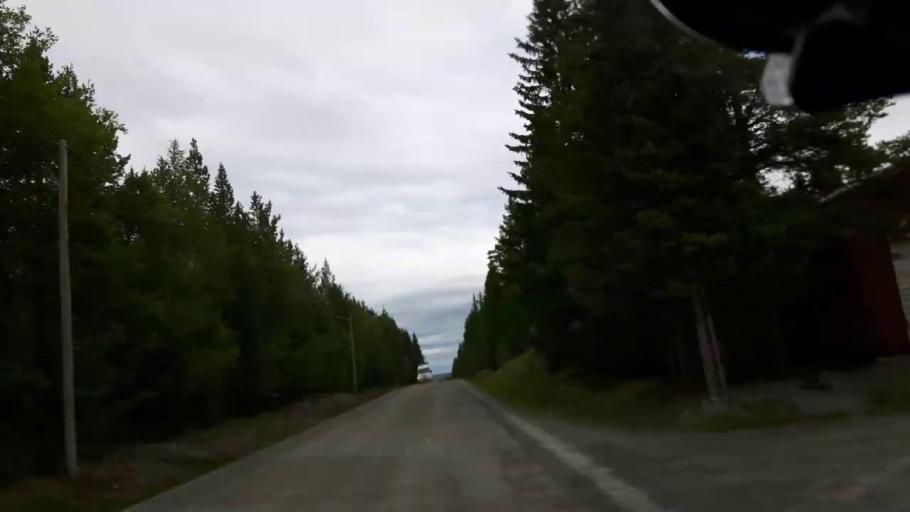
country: SE
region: Jaemtland
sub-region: OEstersunds Kommun
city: Brunflo
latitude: 63.0864
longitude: 14.8790
